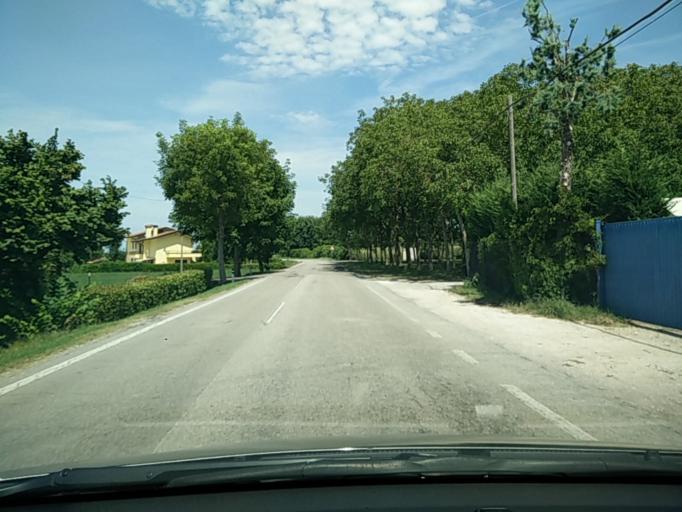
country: IT
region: Veneto
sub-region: Provincia di Venezia
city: Passarella
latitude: 45.5865
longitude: 12.6008
